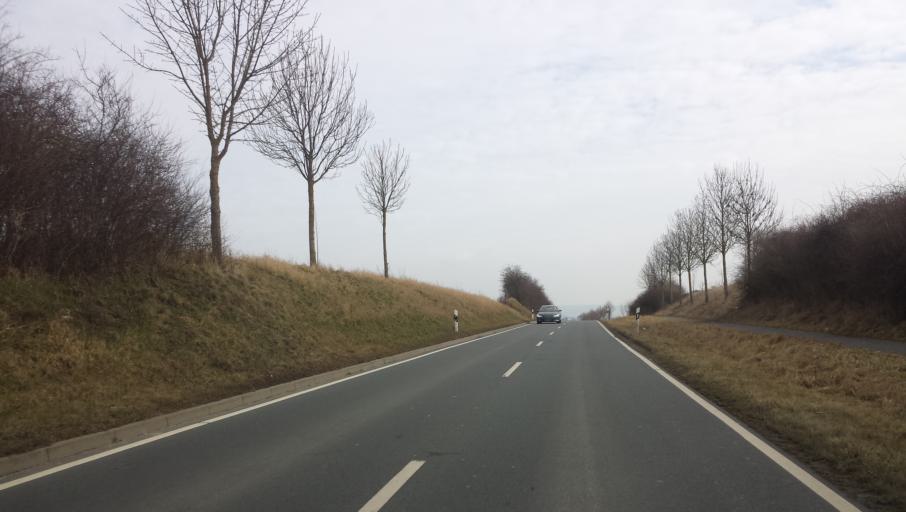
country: DE
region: Hesse
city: Reinheim
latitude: 49.8509
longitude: 8.8618
